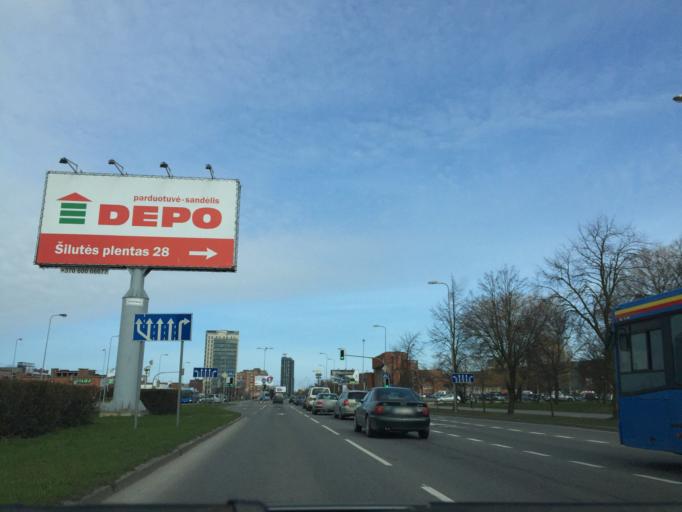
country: LT
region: Klaipedos apskritis
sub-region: Klaipeda
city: Klaipeda
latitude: 55.6888
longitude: 21.1566
